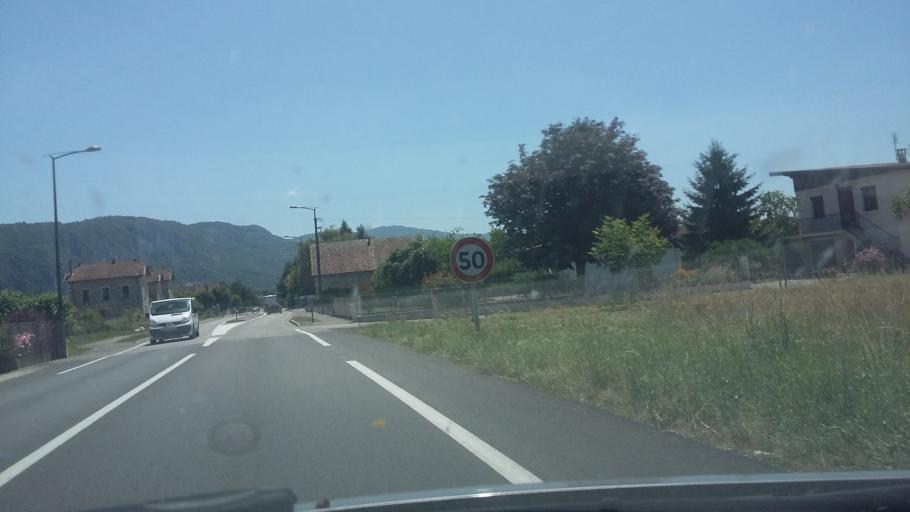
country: FR
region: Rhone-Alpes
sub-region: Departement de l'Ain
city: Belley
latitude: 45.7225
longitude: 5.7098
